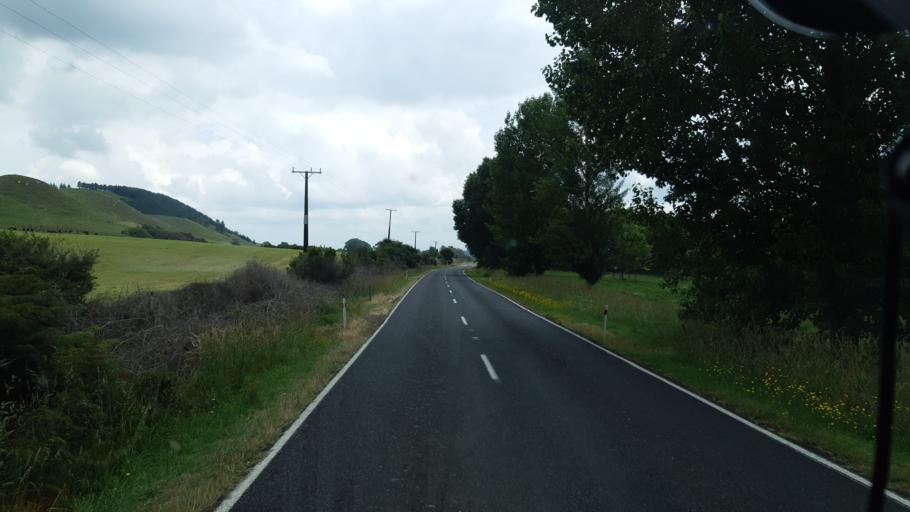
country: NZ
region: Waikato
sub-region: Waipa District
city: Cambridge
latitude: -38.1100
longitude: 175.5029
